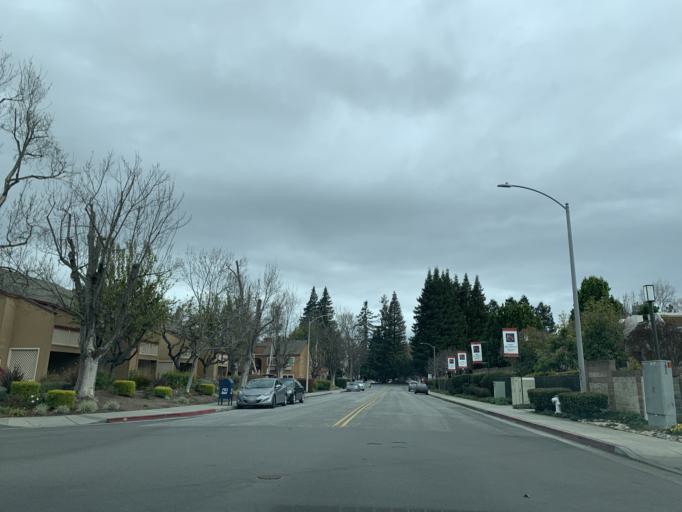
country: US
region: California
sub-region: Santa Clara County
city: Sunnyvale
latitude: 37.3886
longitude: -122.0450
